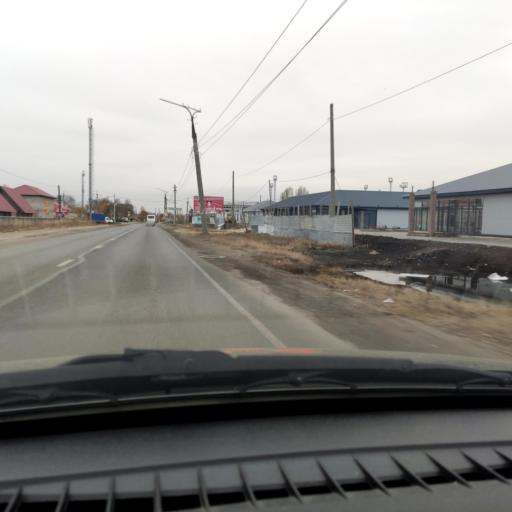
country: RU
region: Samara
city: Tol'yatti
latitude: 53.5092
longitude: 49.2472
